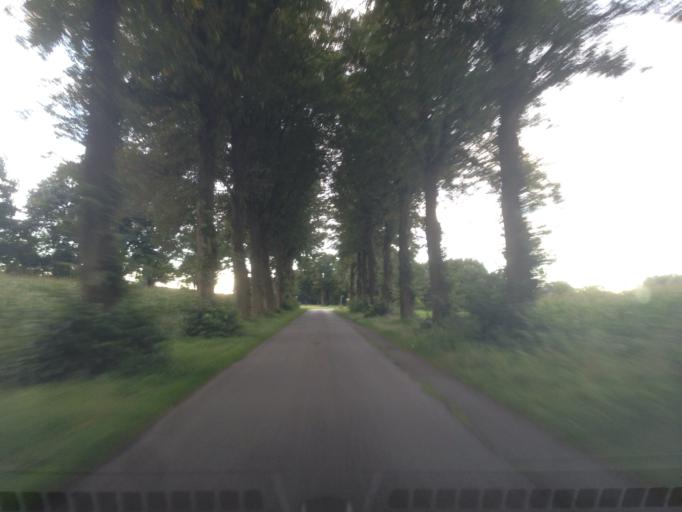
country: DE
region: North Rhine-Westphalia
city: Olfen
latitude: 51.7523
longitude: 7.3901
